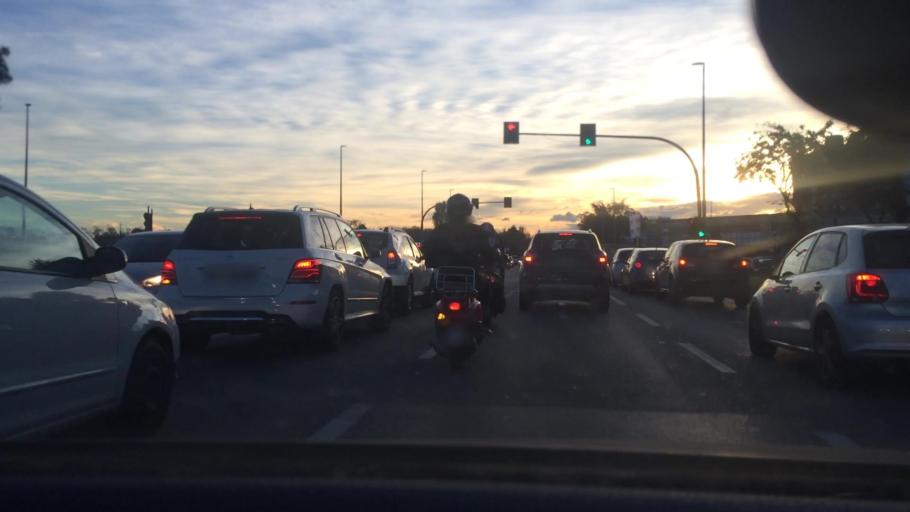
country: IT
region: Lombardy
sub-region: Citta metropolitana di Milano
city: Passirana
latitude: 45.5398
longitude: 9.0336
